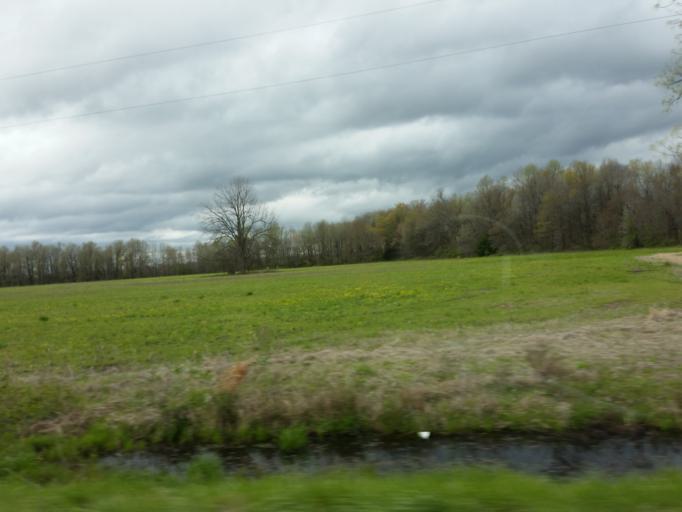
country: US
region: Missouri
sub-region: Butler County
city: Poplar Bluff
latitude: 36.6419
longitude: -90.5203
